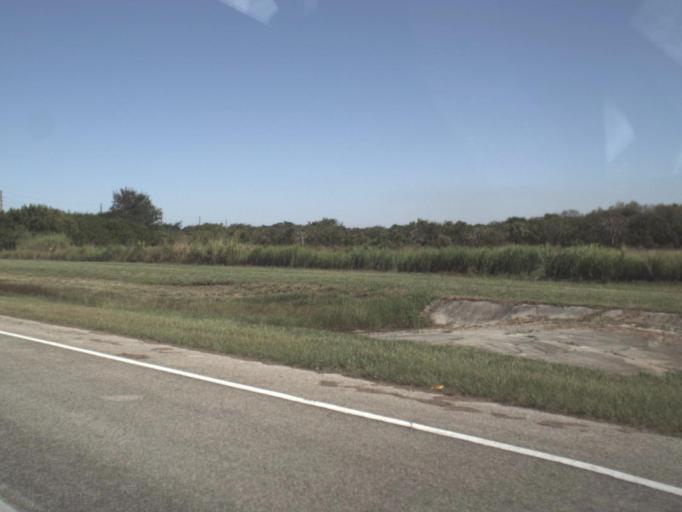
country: US
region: Florida
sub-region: Hendry County
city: LaBelle
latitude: 26.7313
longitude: -81.4793
